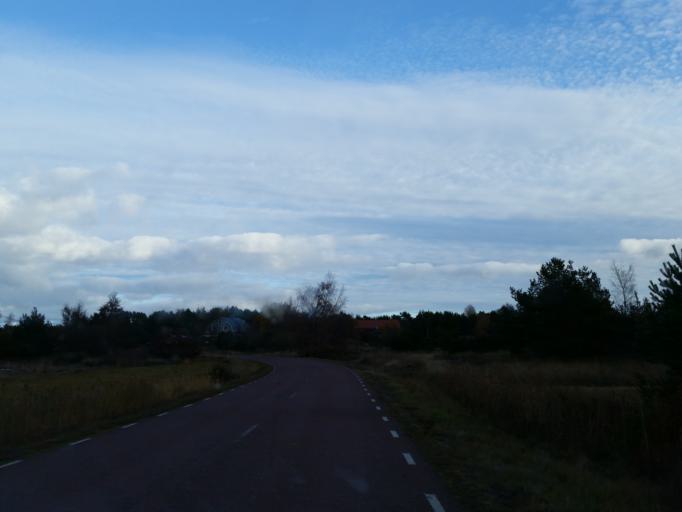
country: AX
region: Alands skaergard
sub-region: Foegloe
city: Foegloe
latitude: 60.0610
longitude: 20.5177
